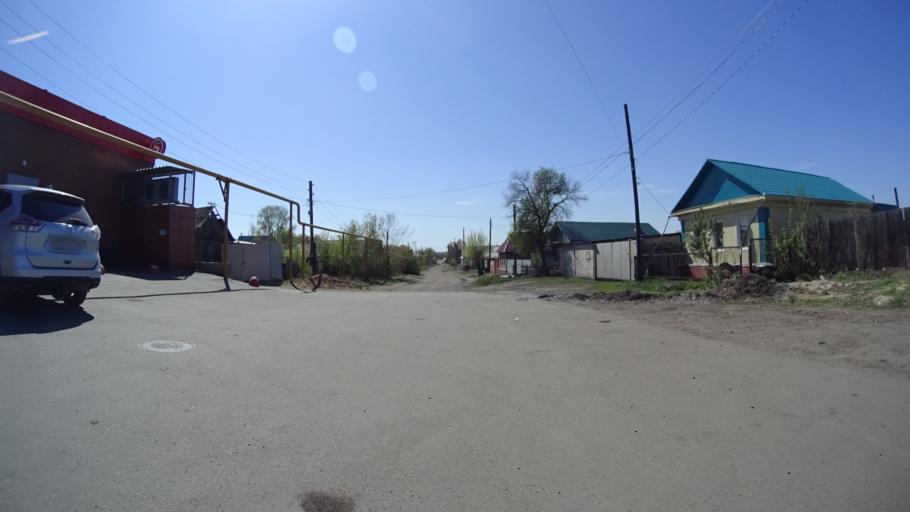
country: RU
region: Chelyabinsk
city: Troitsk
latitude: 54.0954
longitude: 61.5866
